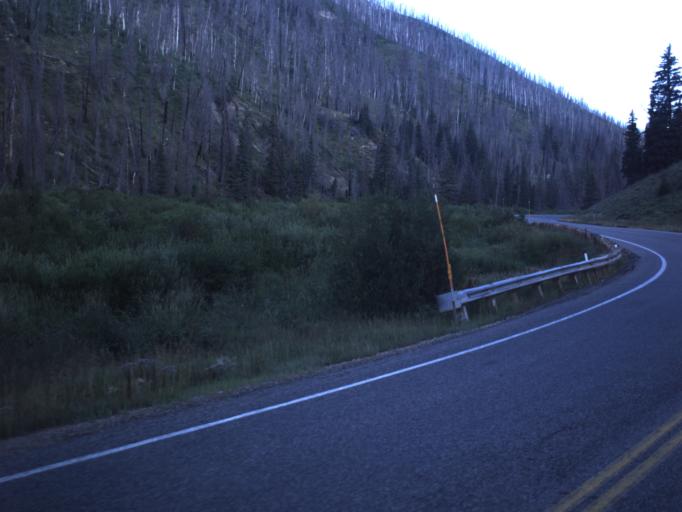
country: US
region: Utah
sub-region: Sanpete County
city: Fairview
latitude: 39.5628
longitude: -111.1757
